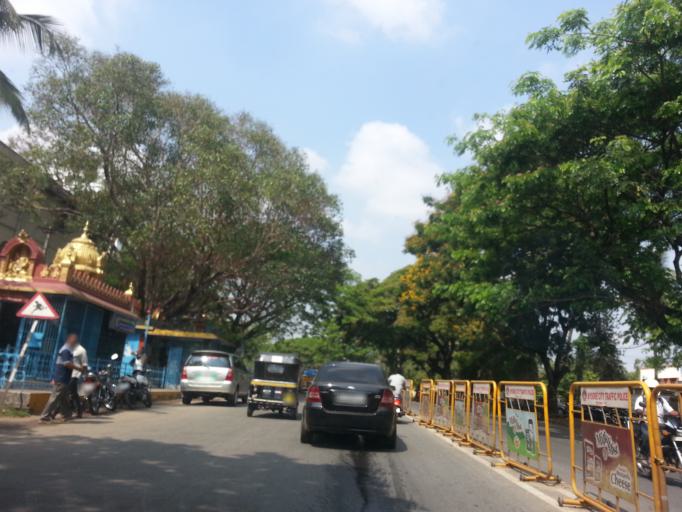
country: IN
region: Karnataka
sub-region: Mysore
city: Mysore
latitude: 12.3320
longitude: 76.6487
